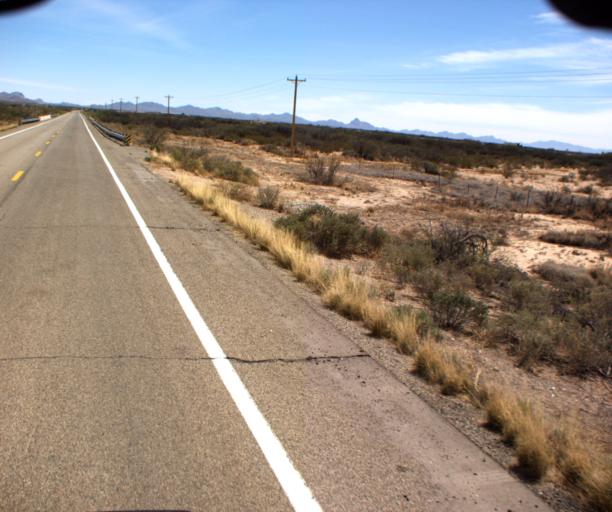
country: US
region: New Mexico
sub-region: Hidalgo County
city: Lordsburg
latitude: 32.2621
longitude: -109.2081
